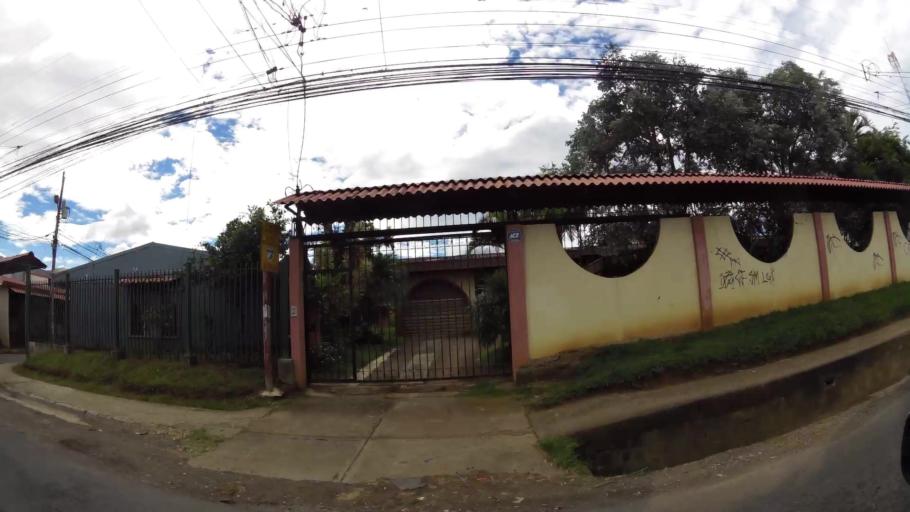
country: CR
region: San Jose
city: San Rafael Arriba
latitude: 9.8876
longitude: -84.0695
